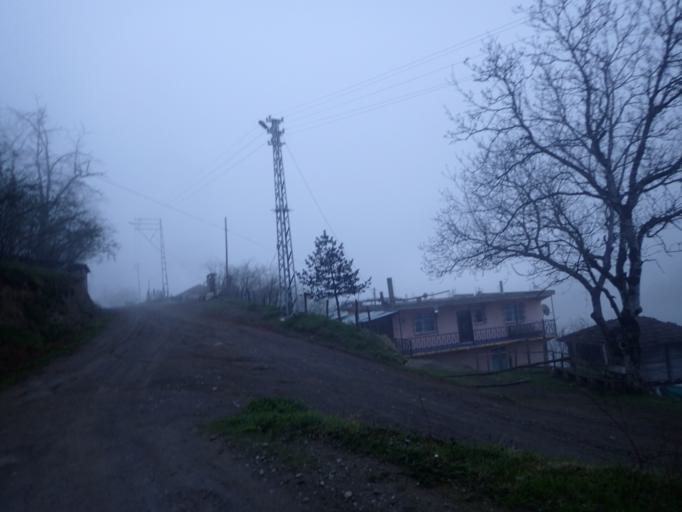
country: TR
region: Ordu
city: Korgan
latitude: 40.7794
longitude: 37.3001
